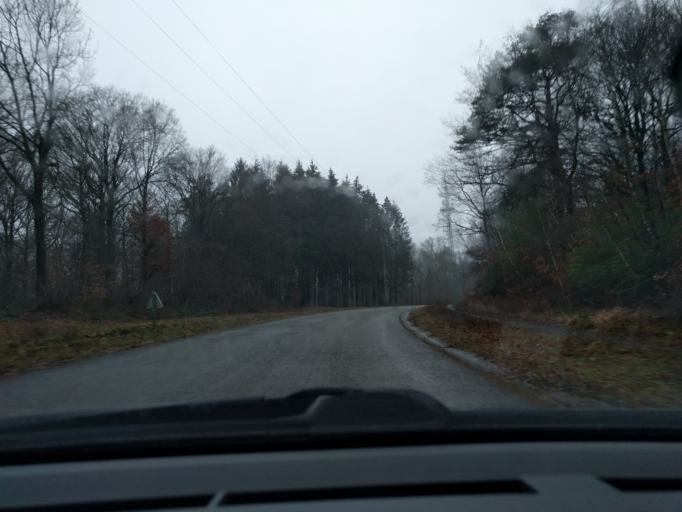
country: BE
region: Wallonia
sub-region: Province de Namur
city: Couvin
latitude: 50.0415
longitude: 4.5356
